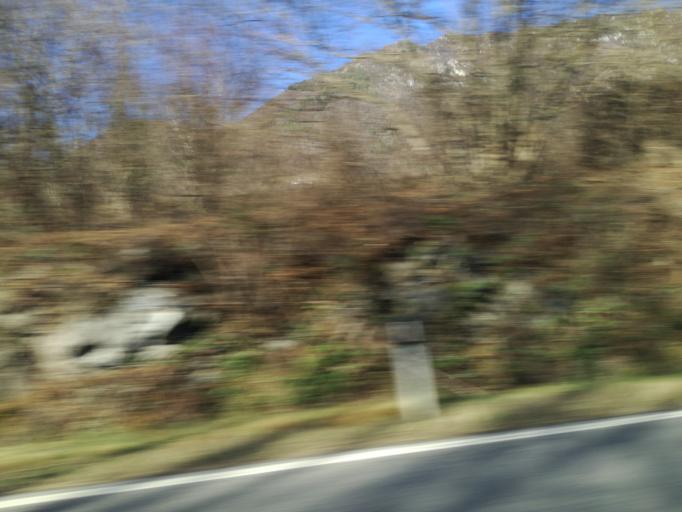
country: IT
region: Lombardy
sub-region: Provincia di Bergamo
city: Piangaiano
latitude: 45.7947
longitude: 10.0096
